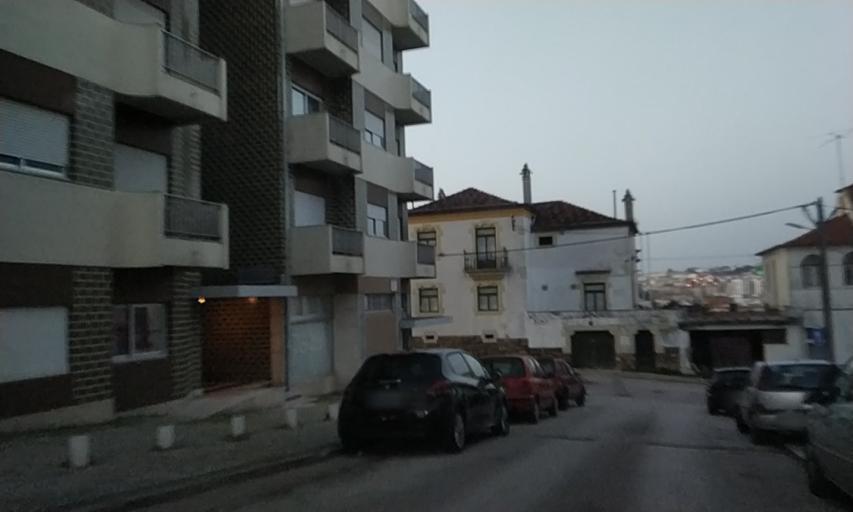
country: PT
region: Leiria
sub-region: Leiria
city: Leiria
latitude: 39.7422
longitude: -8.8064
